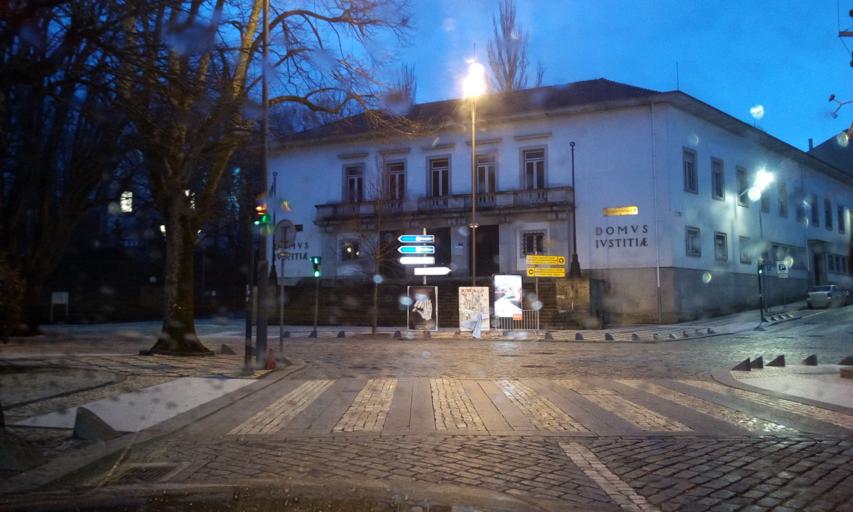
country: PT
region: Viseu
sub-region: Viseu
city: Viseu
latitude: 40.6572
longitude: -7.9147
